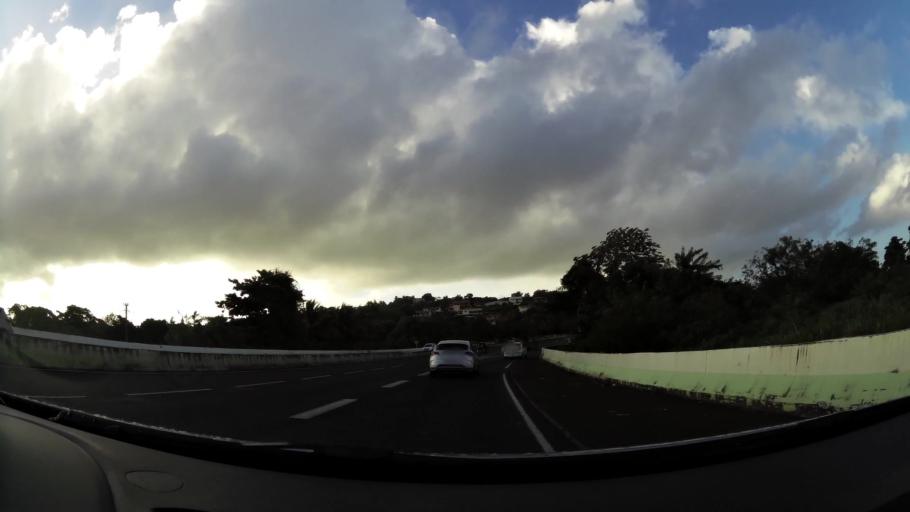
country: MQ
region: Martinique
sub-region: Martinique
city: Ducos
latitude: 14.5831
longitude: -60.9805
